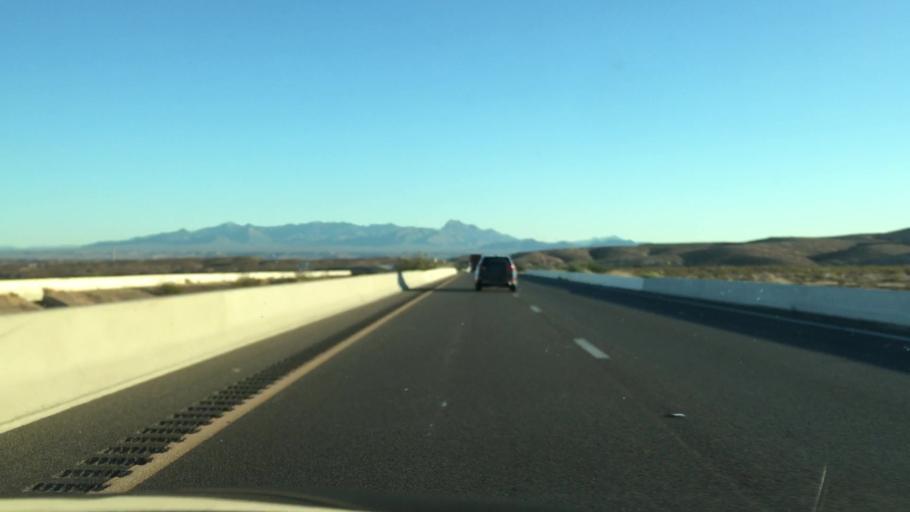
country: US
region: Nevada
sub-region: Clark County
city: Moapa Town
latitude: 36.5905
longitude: -114.6473
